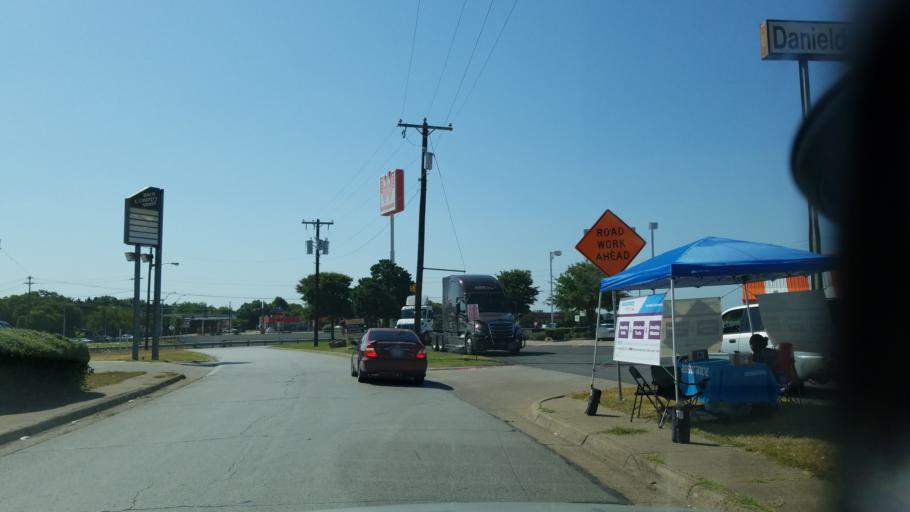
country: US
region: Texas
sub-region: Dallas County
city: Duncanville
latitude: 32.6341
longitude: -96.9008
